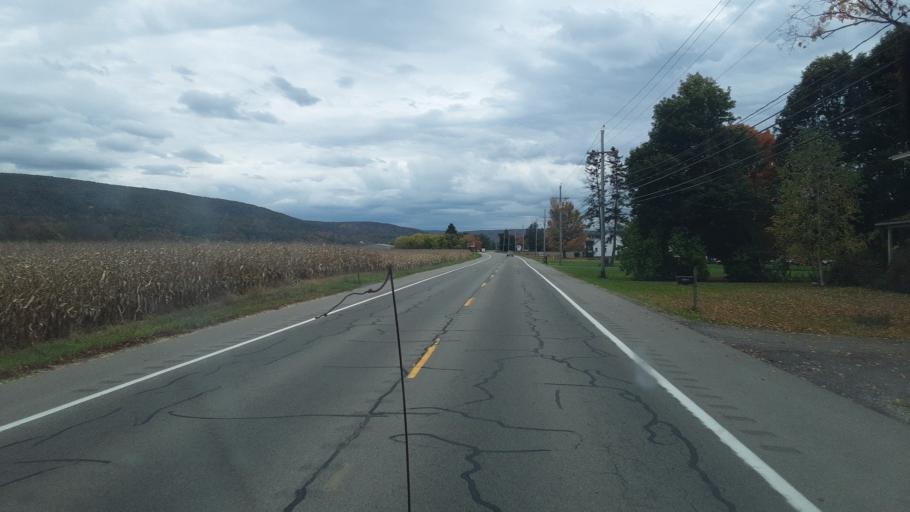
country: US
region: New York
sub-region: Allegany County
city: Belmont
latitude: 42.2072
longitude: -78.0120
